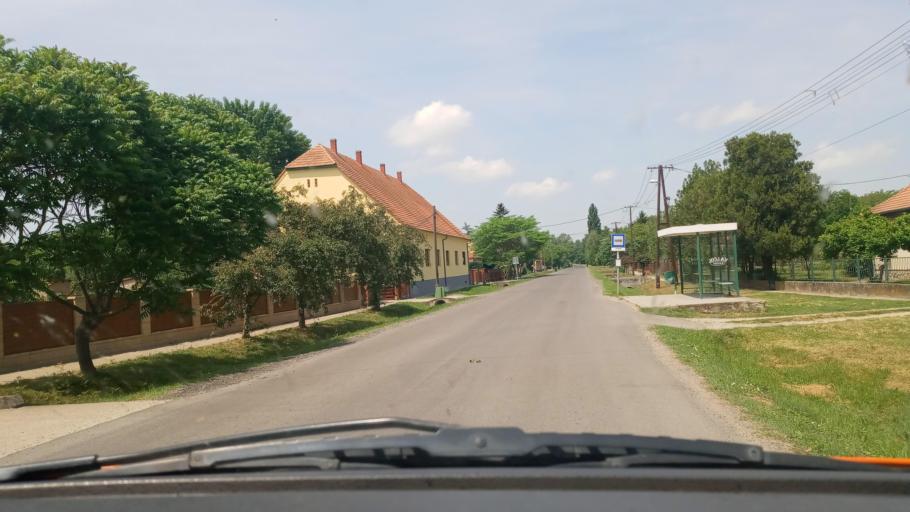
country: HU
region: Baranya
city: Szigetvar
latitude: 45.9751
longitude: 17.7219
